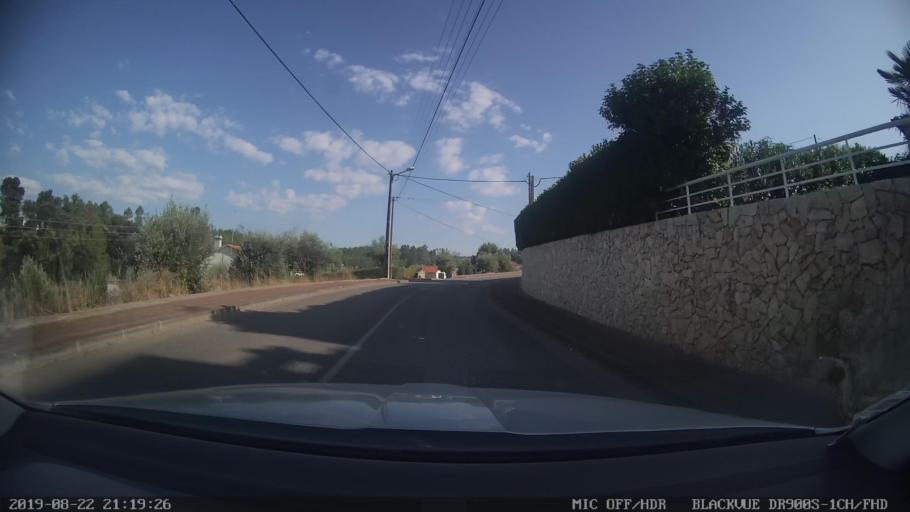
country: PT
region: Castelo Branco
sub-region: Serta
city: Serta
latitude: 39.8055
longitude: -8.1083
